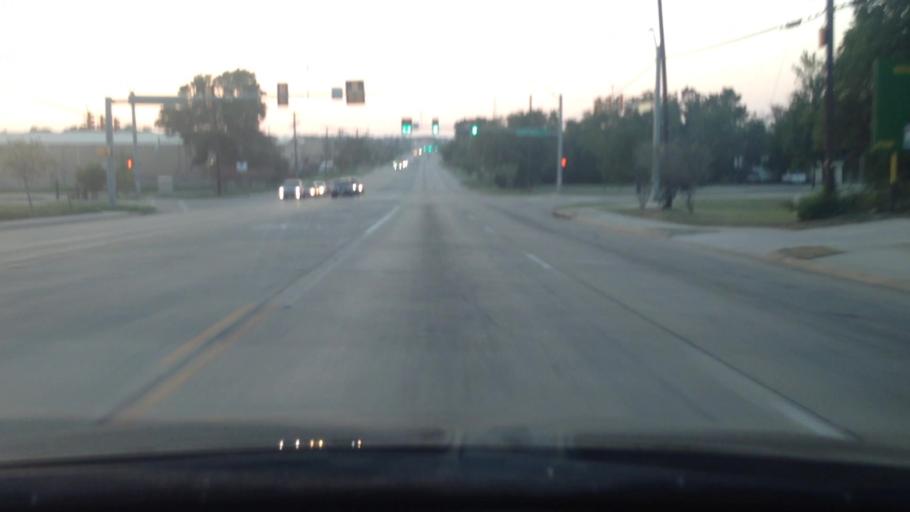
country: US
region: Texas
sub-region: Tarrant County
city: Kennedale
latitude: 32.6544
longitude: -97.2296
